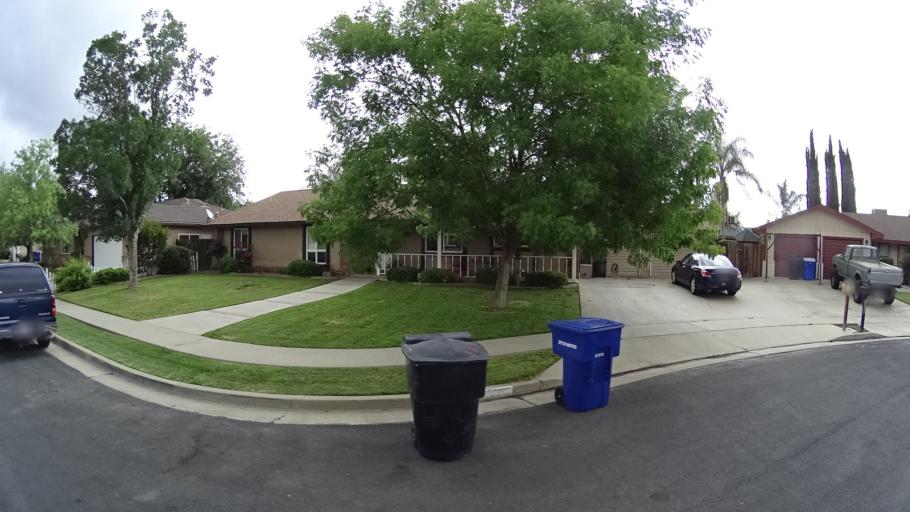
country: US
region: California
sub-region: Kings County
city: Hanford
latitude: 36.3351
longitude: -119.6612
